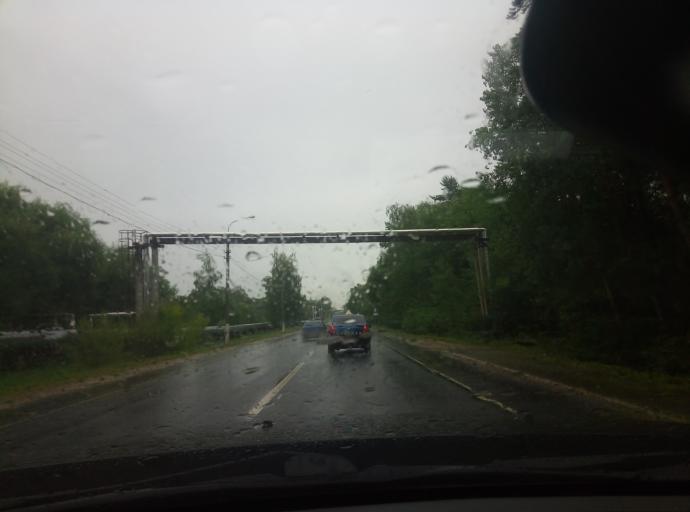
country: RU
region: Moskovskaya
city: Protvino
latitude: 54.8824
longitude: 37.2189
